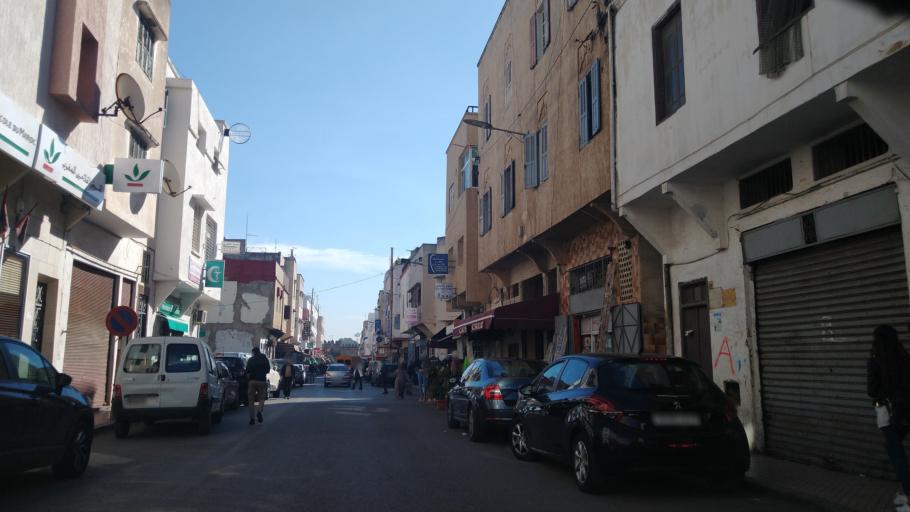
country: MA
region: Rabat-Sale-Zemmour-Zaer
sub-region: Rabat
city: Rabat
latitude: 34.0351
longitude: -6.8220
